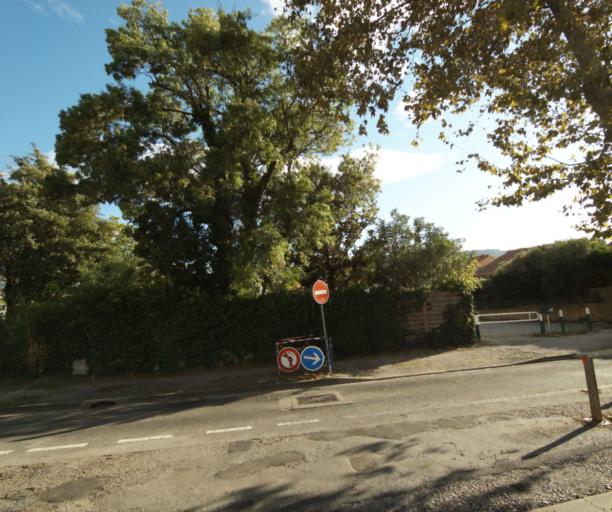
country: FR
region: Languedoc-Roussillon
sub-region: Departement des Pyrenees-Orientales
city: Argelers
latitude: 42.5502
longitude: 3.0399
